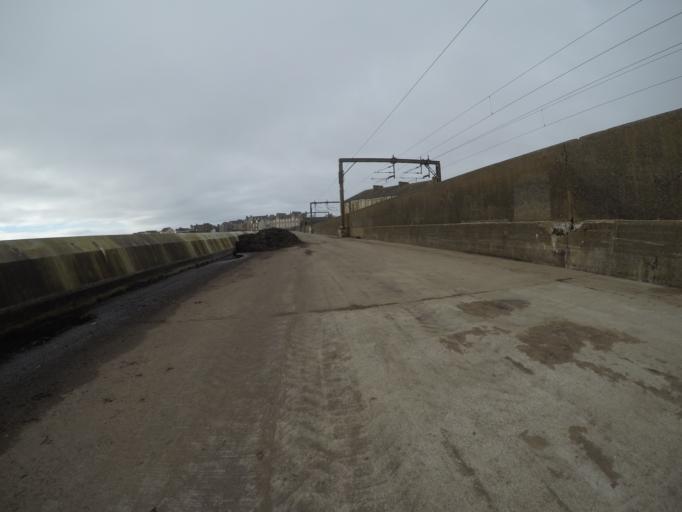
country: GB
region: Scotland
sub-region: North Ayrshire
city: Saltcoats
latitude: 55.6333
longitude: -4.7791
